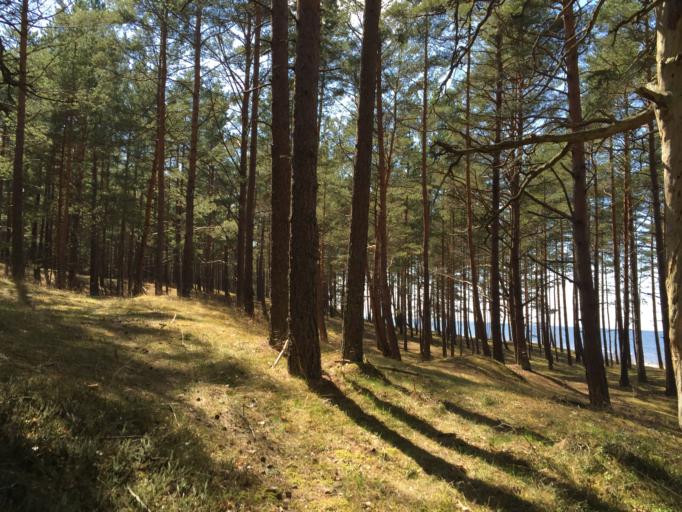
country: LV
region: Saulkrastu
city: Saulkrasti
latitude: 57.2291
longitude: 24.3863
